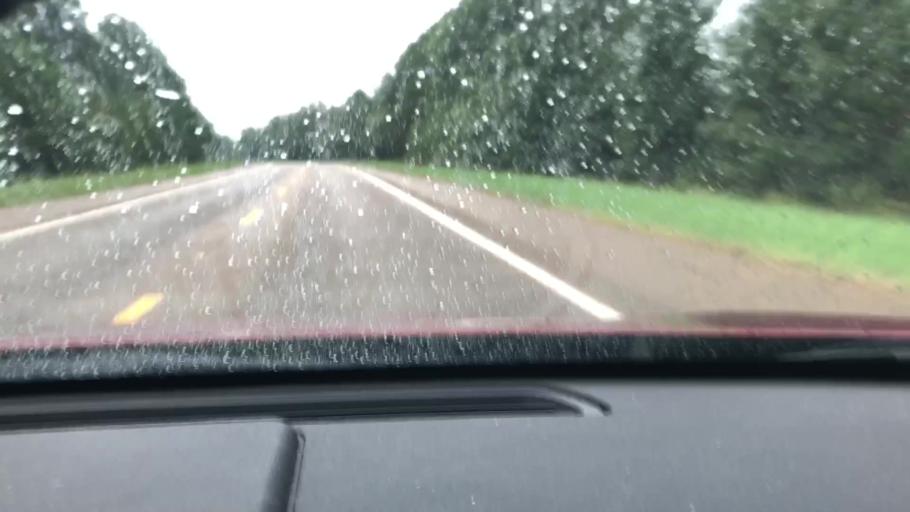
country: US
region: Arkansas
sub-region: Columbia County
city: Magnolia
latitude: 33.2981
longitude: -93.2622
